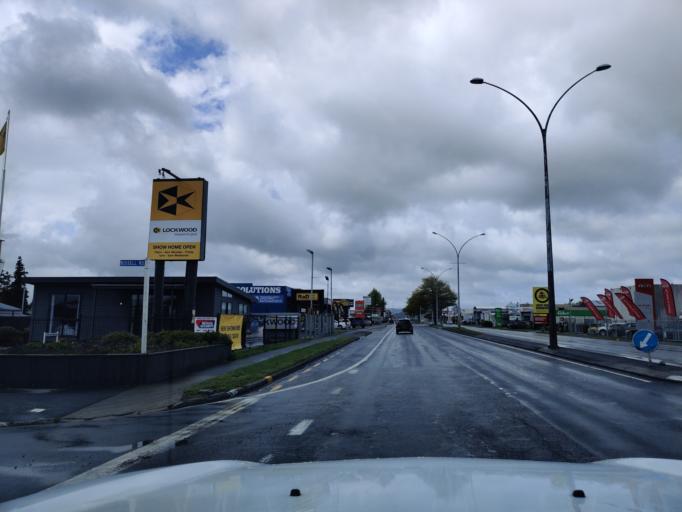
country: NZ
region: Bay of Plenty
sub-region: Rotorua District
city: Rotorua
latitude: -38.1205
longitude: 176.2290
